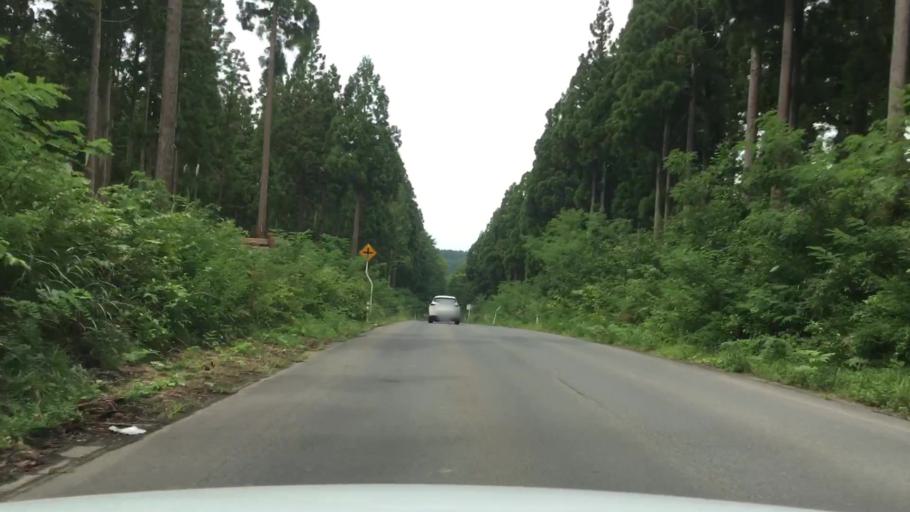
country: JP
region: Aomori
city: Shimokizukuri
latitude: 40.7115
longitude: 140.2695
